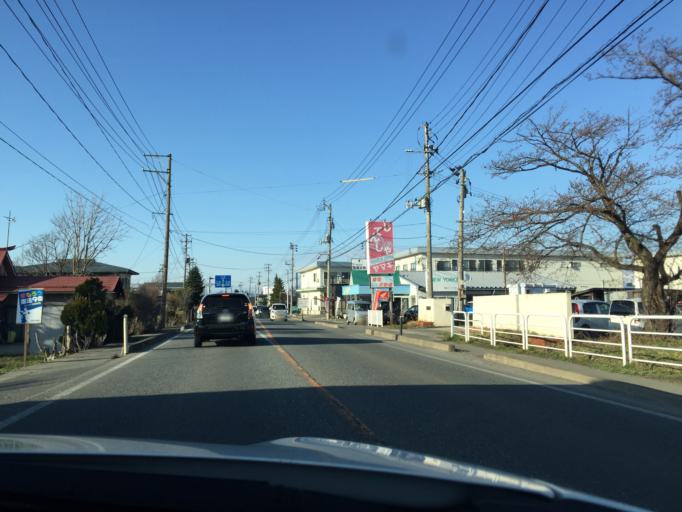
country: JP
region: Yamagata
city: Yonezawa
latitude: 37.9542
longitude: 140.1247
